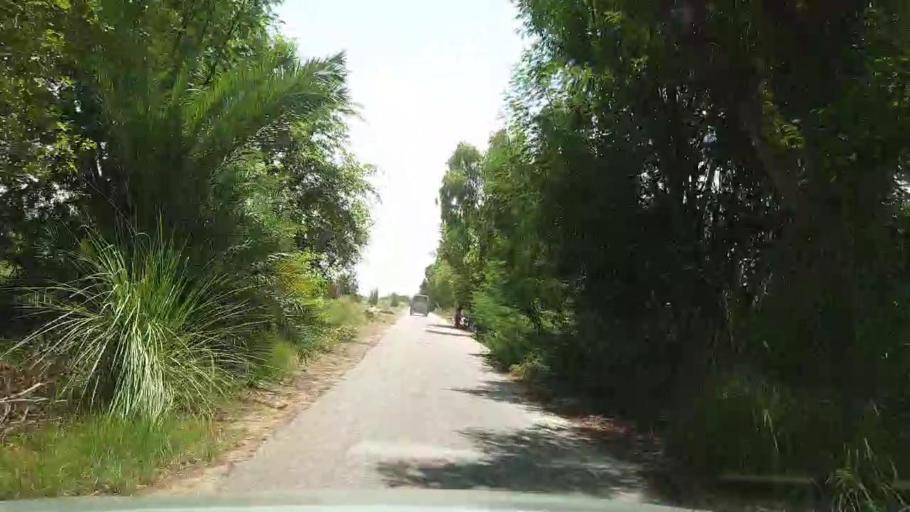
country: PK
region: Sindh
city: Bozdar
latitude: 27.0722
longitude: 68.9757
